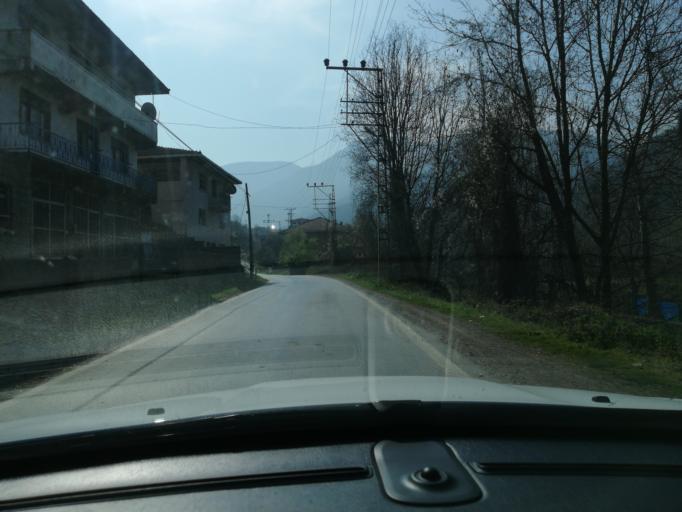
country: TR
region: Karabuk
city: Yenice
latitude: 41.2125
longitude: 32.3640
